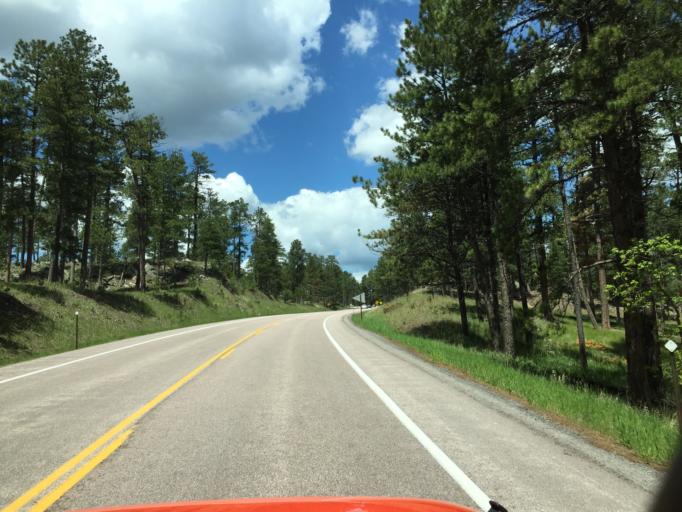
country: US
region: South Dakota
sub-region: Custer County
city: Custer
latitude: 43.8962
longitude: -103.4817
